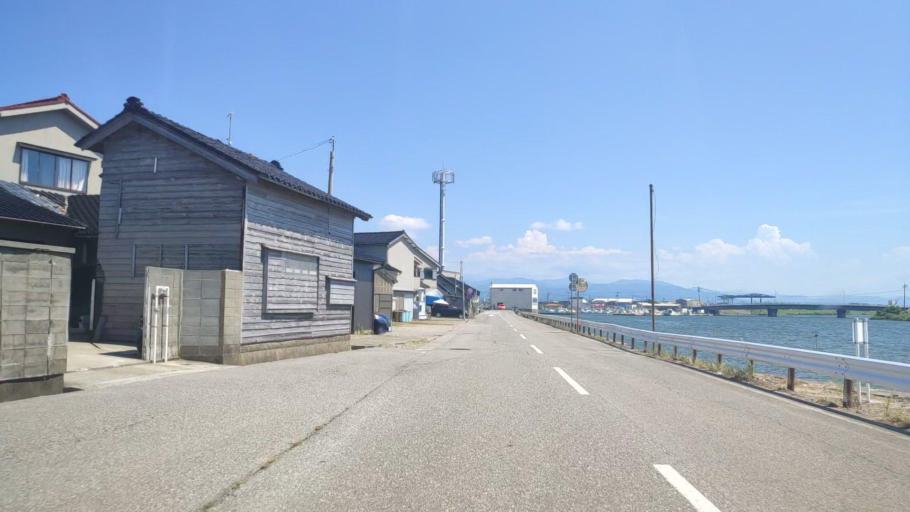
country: JP
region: Ishikawa
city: Kanazawa-shi
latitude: 36.6003
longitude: 136.5889
